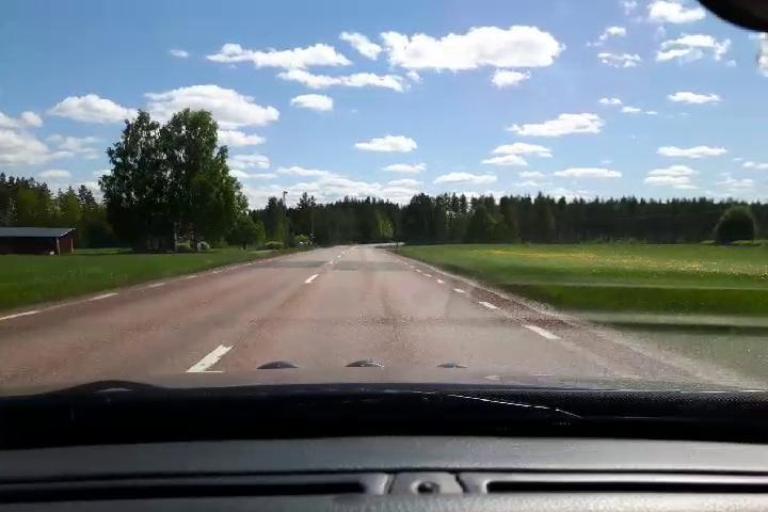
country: SE
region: Gaevleborg
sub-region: Ljusdals Kommun
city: Farila
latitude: 61.8399
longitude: 15.7511
